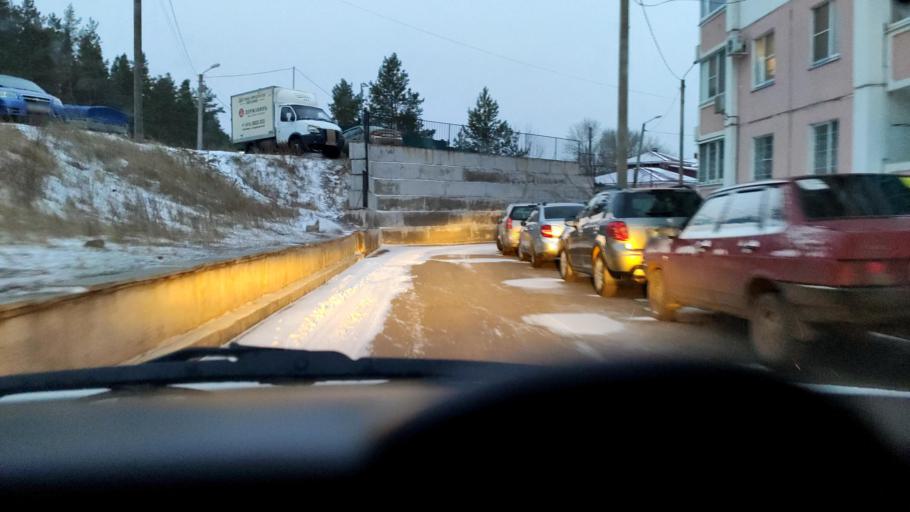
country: RU
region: Voronezj
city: Pridonskoy
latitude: 51.7057
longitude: 39.1074
